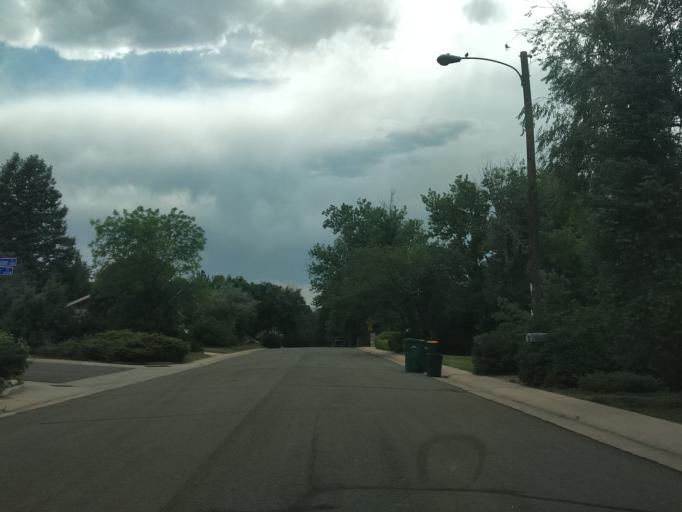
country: US
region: Colorado
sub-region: Jefferson County
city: Lakewood
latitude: 39.6989
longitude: -105.0930
